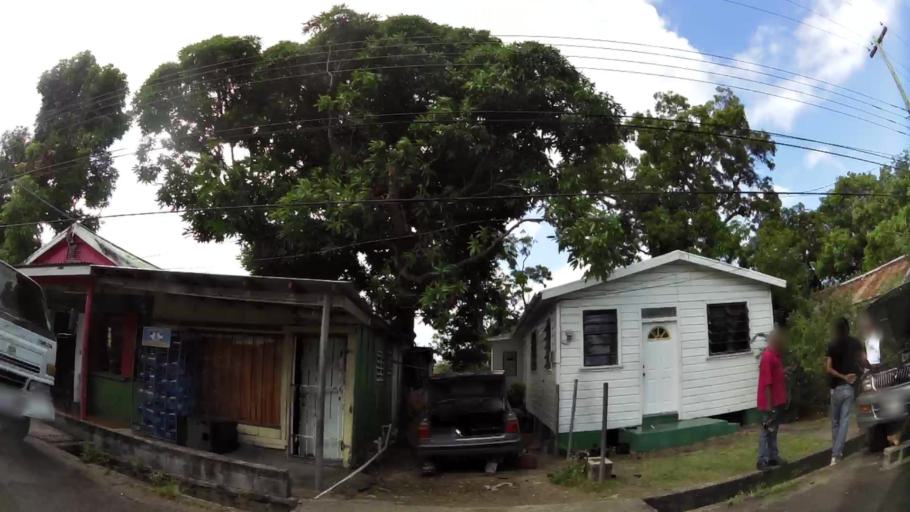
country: AG
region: Saint John
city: Saint John's
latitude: 17.1115
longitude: -61.8447
